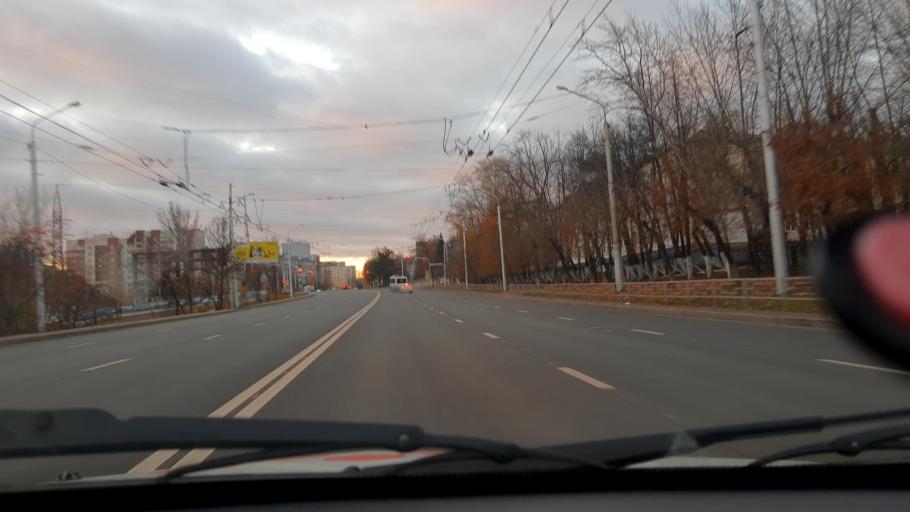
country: RU
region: Bashkortostan
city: Ufa
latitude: 54.7750
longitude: 56.0344
